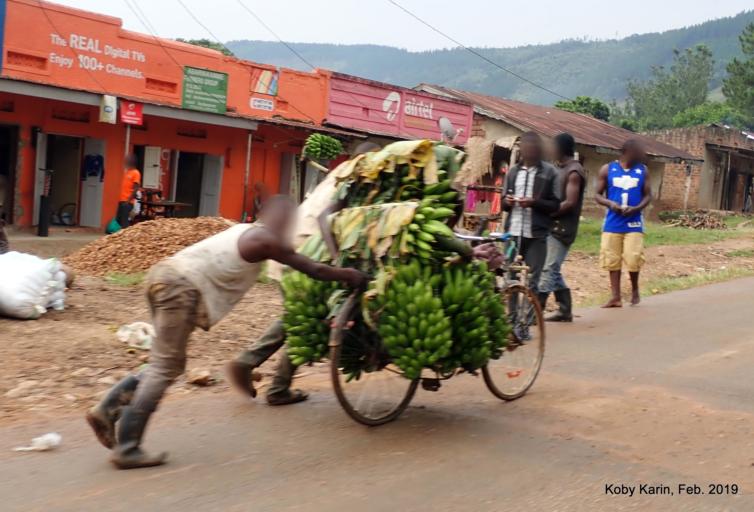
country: UG
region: Western Region
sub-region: Rubirizi District
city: Rubirizi
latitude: -0.3327
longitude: 30.0985
